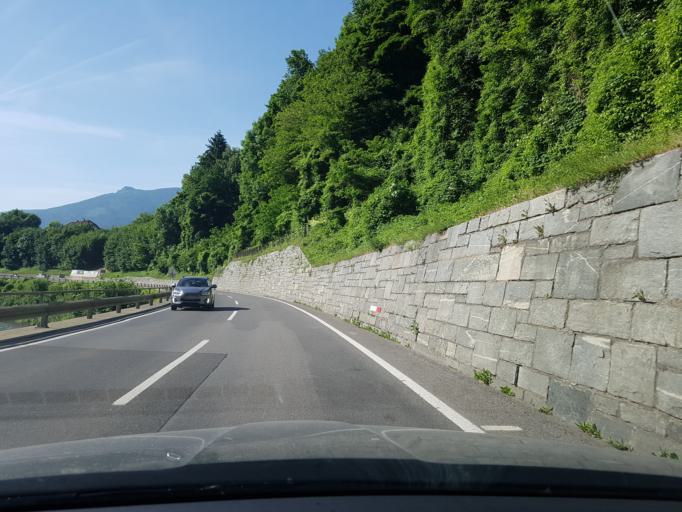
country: AT
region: Carinthia
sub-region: Politischer Bezirk Spittal an der Drau
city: Spittal an der Drau
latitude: 46.8039
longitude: 13.4956
